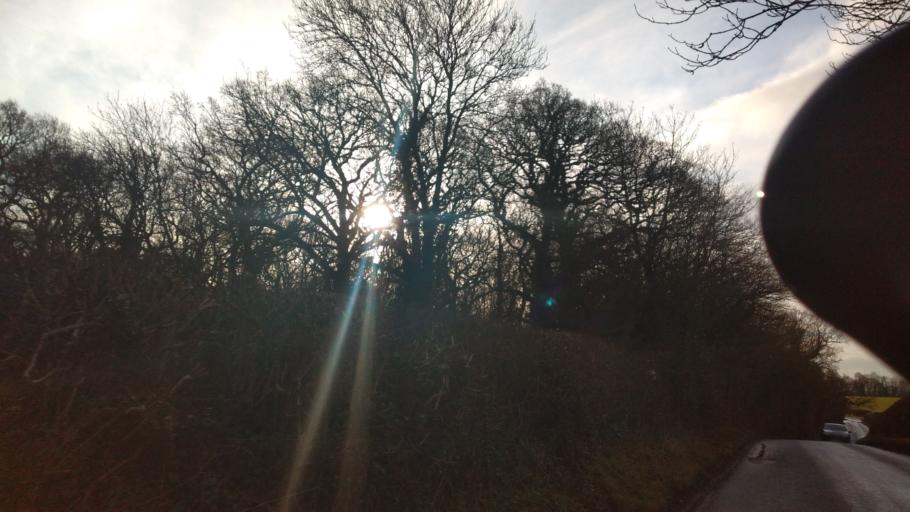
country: GB
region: England
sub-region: Wiltshire
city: Biddestone
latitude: 51.4506
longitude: -2.1876
